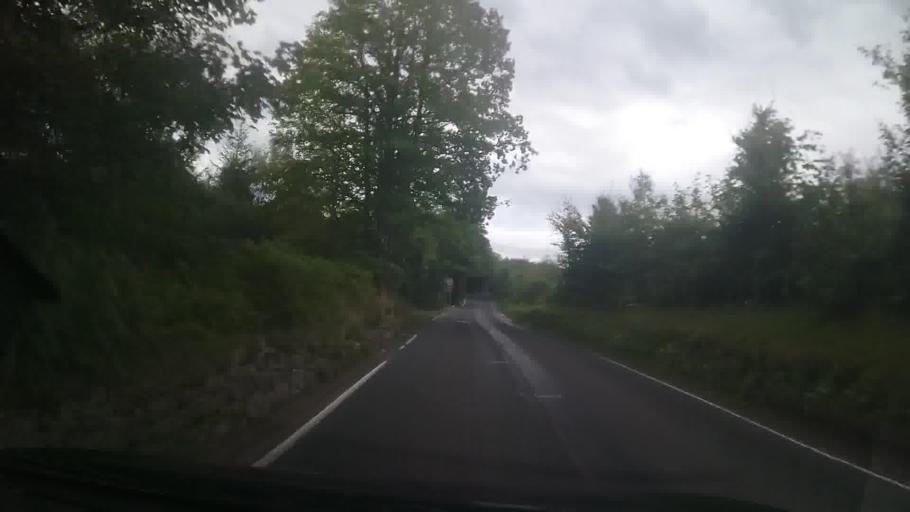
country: GB
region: Scotland
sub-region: Argyll and Bute
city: Garelochhead
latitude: 56.2408
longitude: -5.0854
